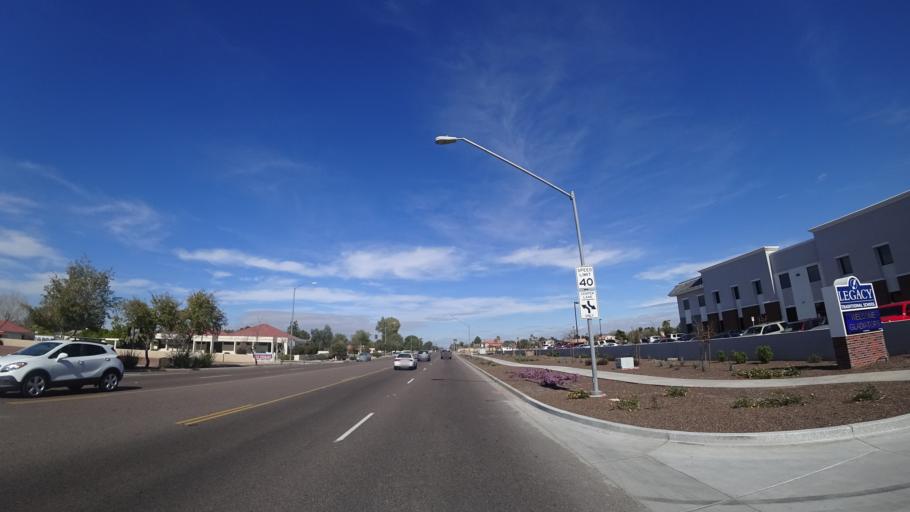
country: US
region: Arizona
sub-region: Maricopa County
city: Peoria
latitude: 33.6119
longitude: -112.2025
